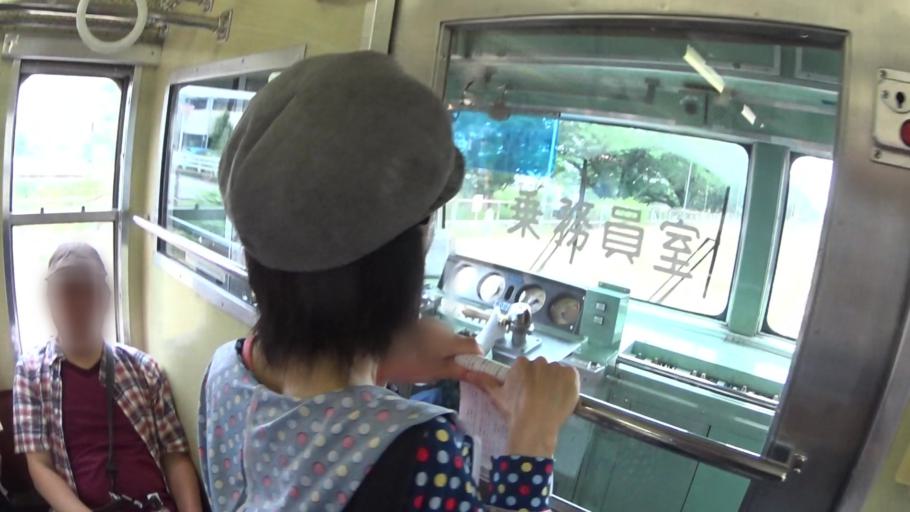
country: JP
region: Chiba
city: Nagareyama
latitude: 35.8249
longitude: 139.9184
